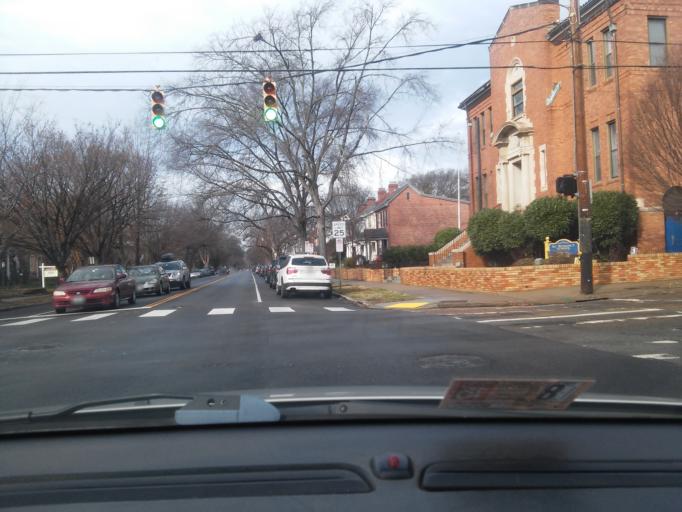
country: US
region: Virginia
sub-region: City of Richmond
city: Richmond
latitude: 37.5563
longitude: -77.4781
